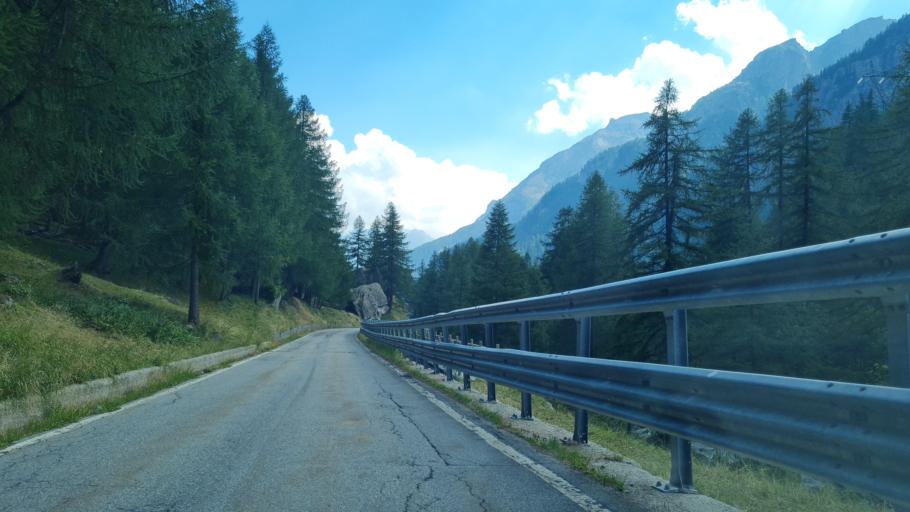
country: IT
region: Piedmont
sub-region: Provincia Verbano-Cusio-Ossola
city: Formazza
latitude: 46.4009
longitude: 8.4199
